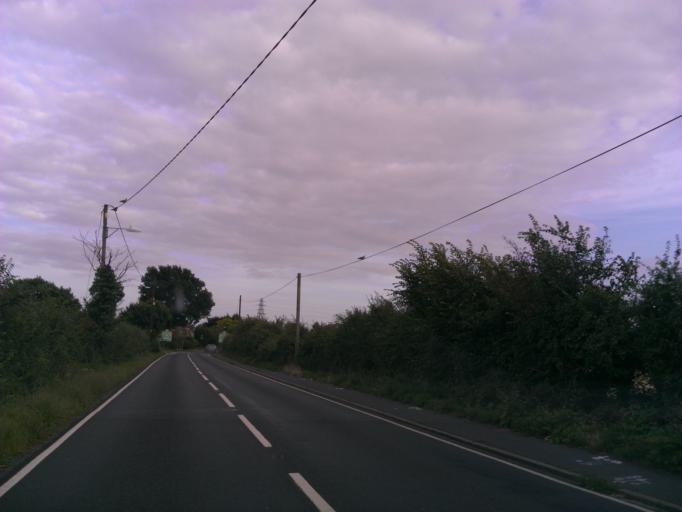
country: GB
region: England
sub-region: Essex
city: Wivenhoe
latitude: 51.8726
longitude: 0.9613
